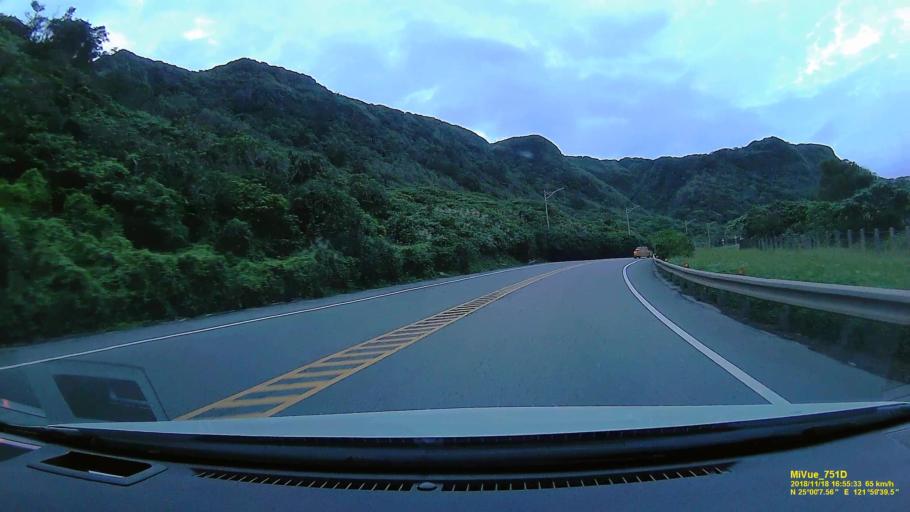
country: TW
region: Taiwan
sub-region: Keelung
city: Keelung
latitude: 25.0021
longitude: 121.9940
